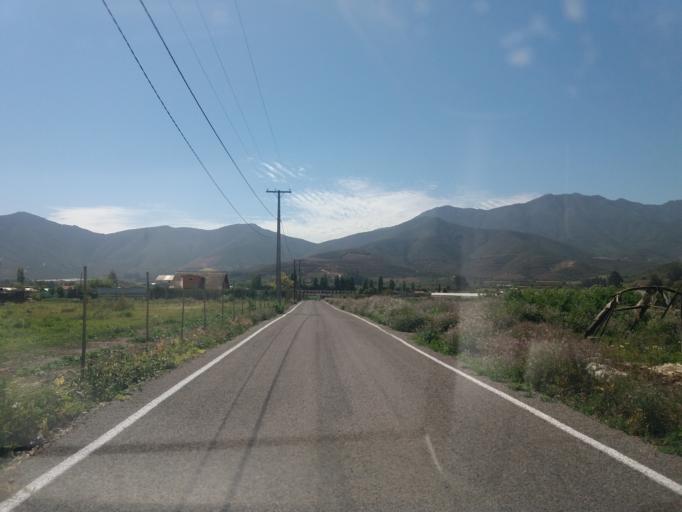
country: CL
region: Valparaiso
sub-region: Provincia de Quillota
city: Quillota
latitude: -32.8571
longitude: -71.2083
